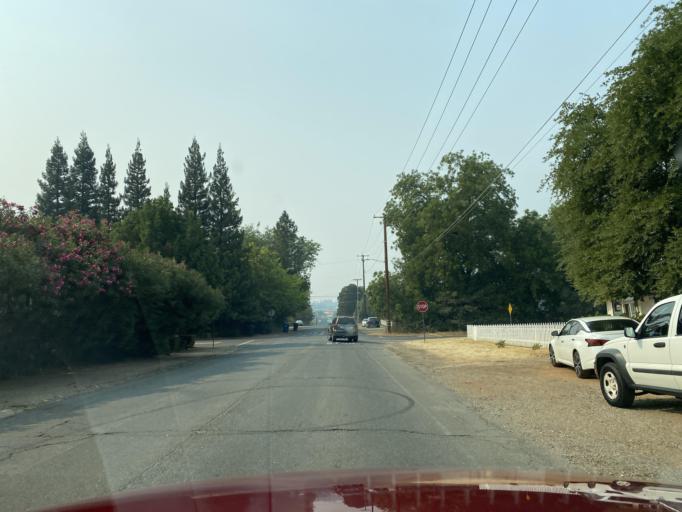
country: US
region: California
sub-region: Sacramento County
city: Folsom
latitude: 38.6789
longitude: -121.1714
